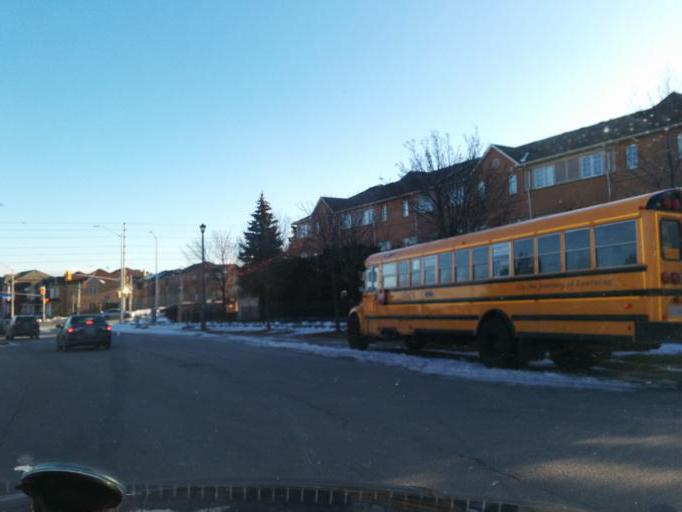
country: CA
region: Ontario
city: Mississauga
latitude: 43.5906
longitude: -79.6727
